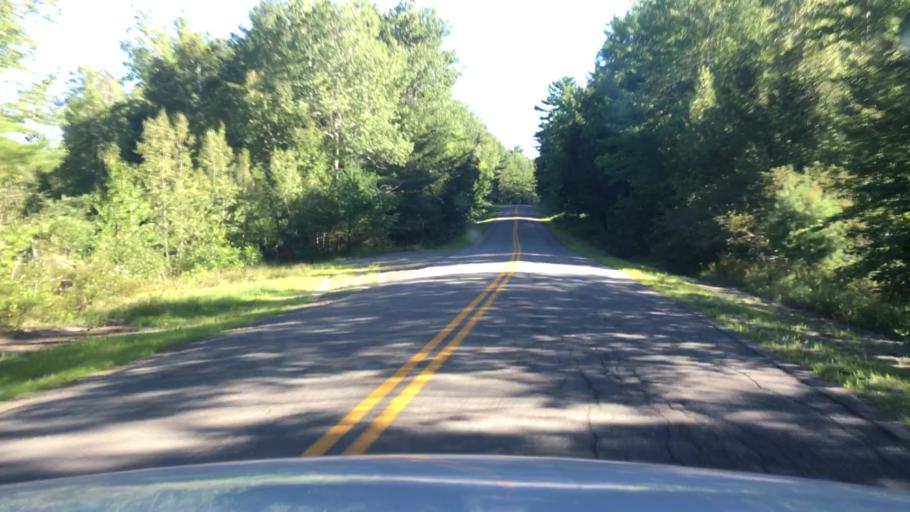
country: US
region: Maine
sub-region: Penobscot County
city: Enfield
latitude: 45.2254
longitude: -68.5801
